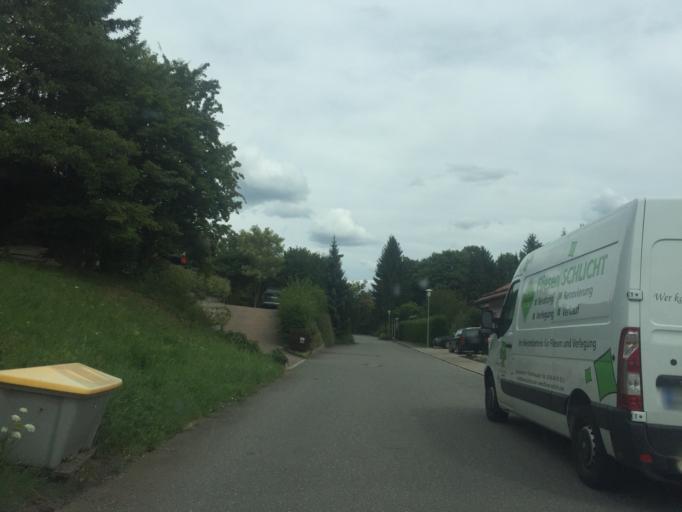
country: DE
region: Bavaria
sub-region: Upper Palatinate
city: Pressath
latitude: 49.7731
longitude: 11.9411
